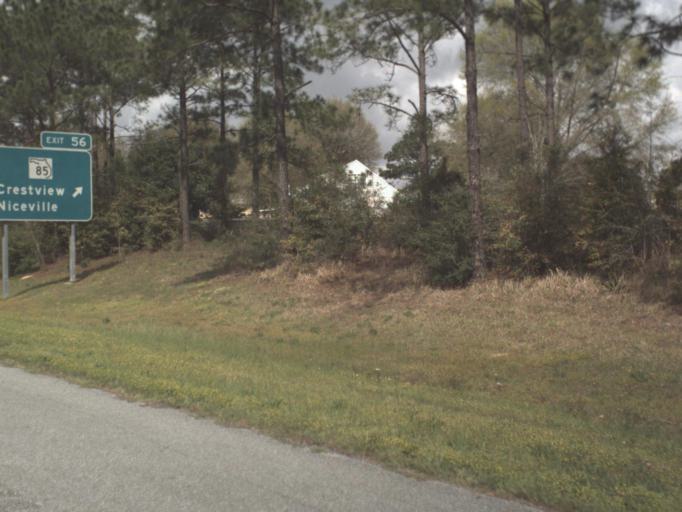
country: US
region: Florida
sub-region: Okaloosa County
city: Crestview
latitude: 30.7261
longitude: -86.5624
